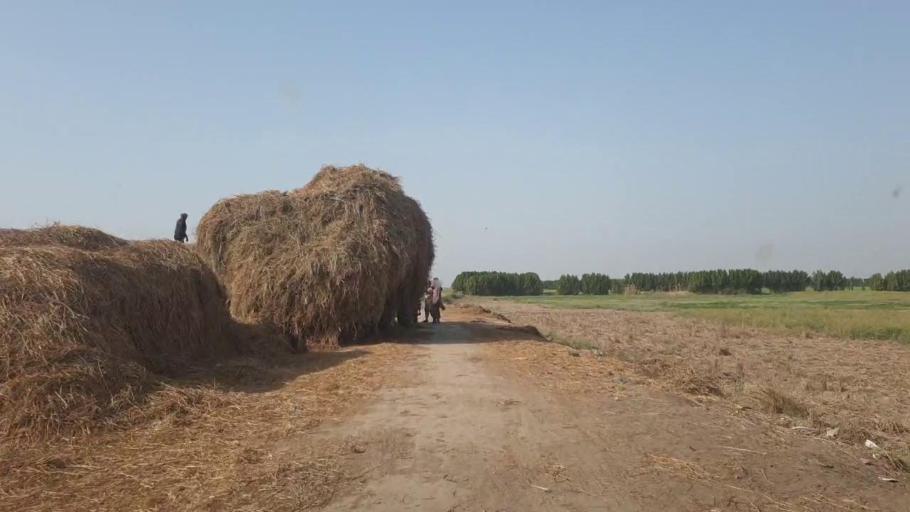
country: PK
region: Sindh
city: Kario
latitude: 24.5801
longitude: 68.5442
